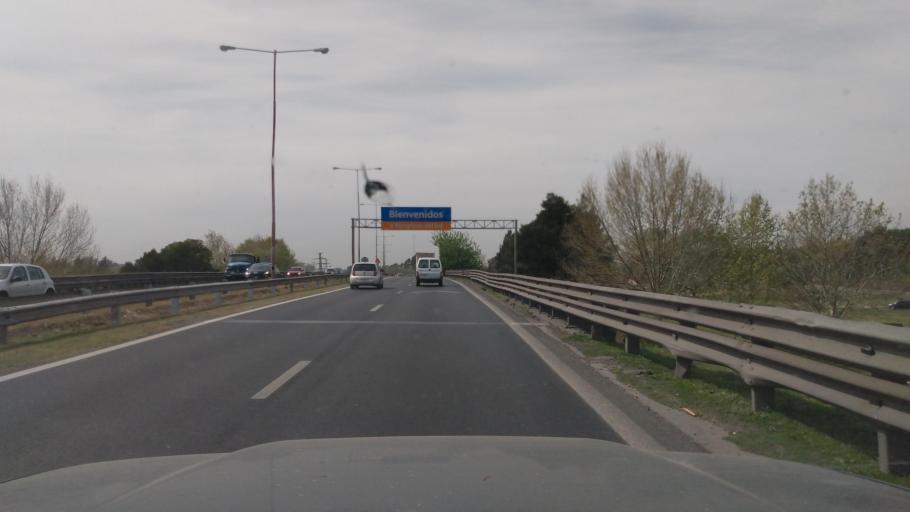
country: AR
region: Buenos Aires
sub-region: Partido de Pilar
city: Pilar
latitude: -34.4535
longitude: -58.9408
